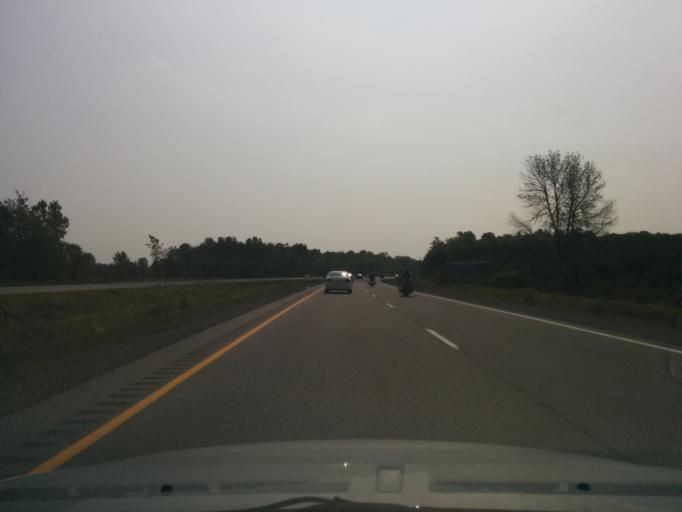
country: CA
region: Ontario
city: Bells Corners
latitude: 45.1643
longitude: -75.6907
